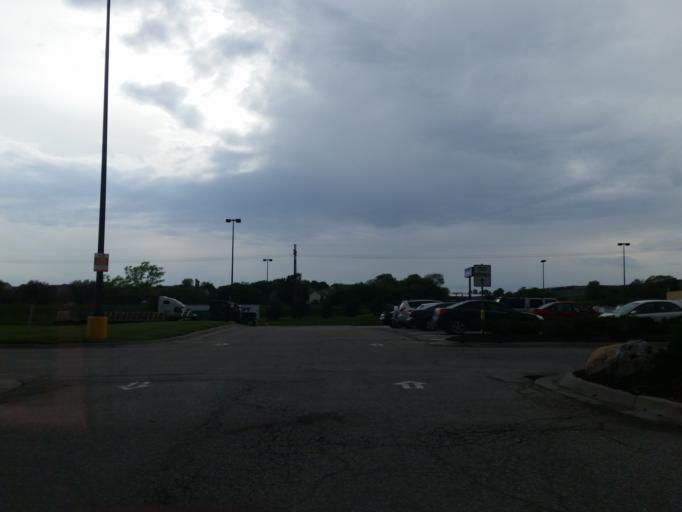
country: US
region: Nebraska
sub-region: Sarpy County
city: Offutt Air Force Base
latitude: 41.1543
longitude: -95.9356
